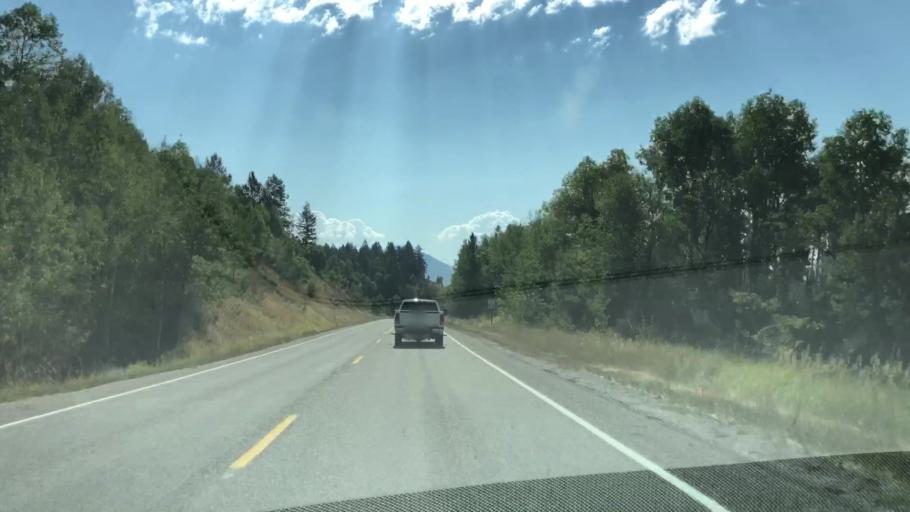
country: US
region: Wyoming
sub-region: Teton County
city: Hoback
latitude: 43.2315
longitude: -111.0918
